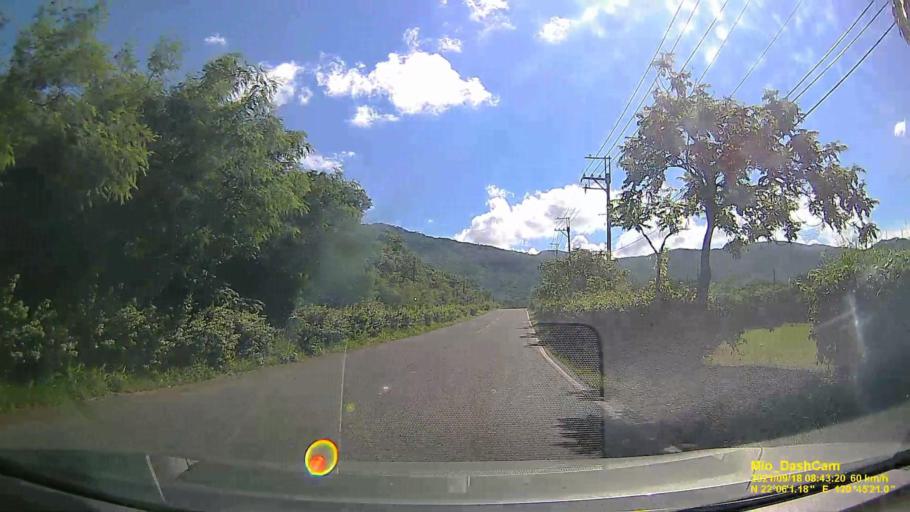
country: TW
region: Taiwan
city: Hengchun
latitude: 22.1003
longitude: 120.7558
